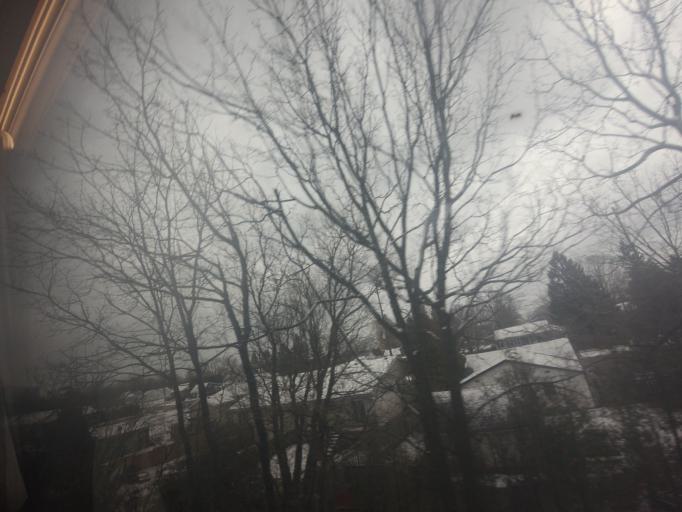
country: CA
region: Ontario
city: Cobourg
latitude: 43.9475
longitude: -78.2895
